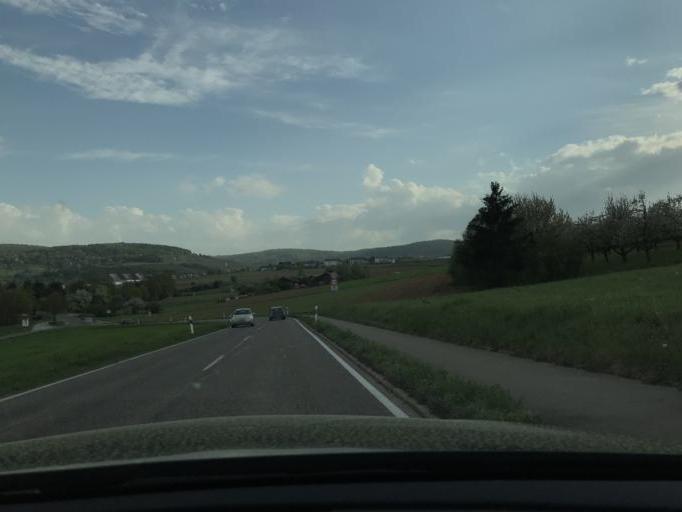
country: DE
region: Baden-Wuerttemberg
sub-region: Regierungsbezirk Stuttgart
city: Weinstadt-Endersbach
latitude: 48.8061
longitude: 9.3503
